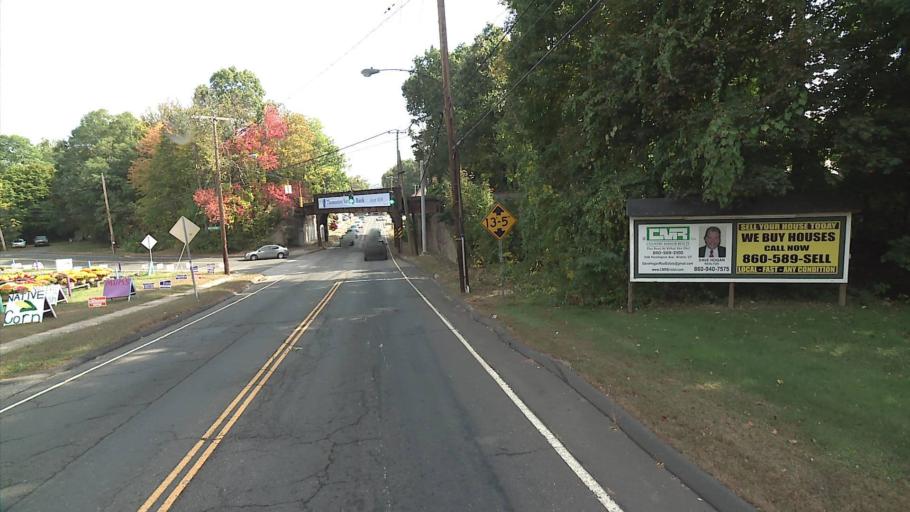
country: US
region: Connecticut
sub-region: Hartford County
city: Bristol
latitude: 41.6810
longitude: -72.9578
